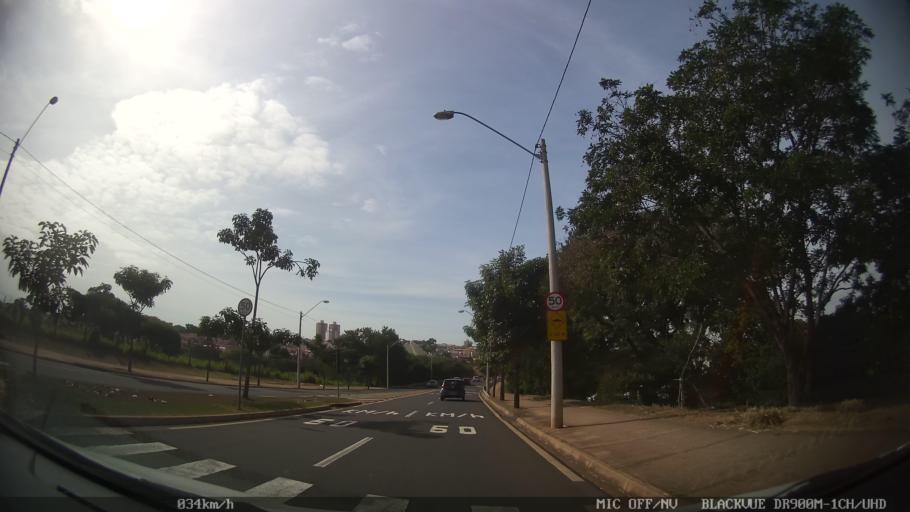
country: BR
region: Sao Paulo
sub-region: Piracicaba
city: Piracicaba
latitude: -22.7468
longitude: -47.6281
